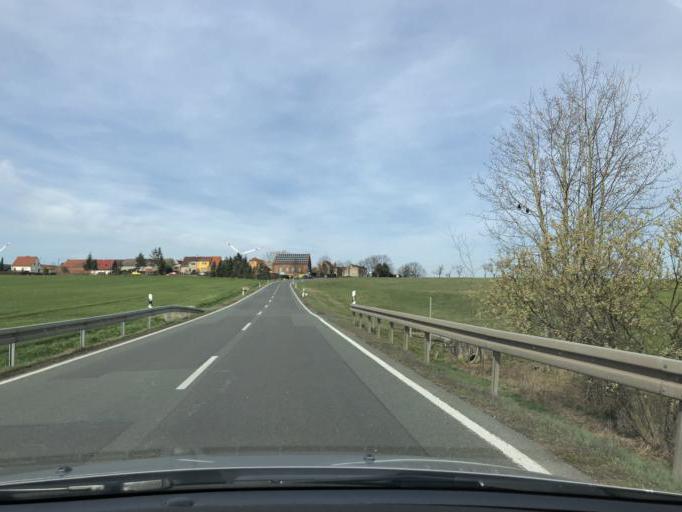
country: DE
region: Thuringia
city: Walpernhain
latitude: 51.0162
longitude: 11.9196
